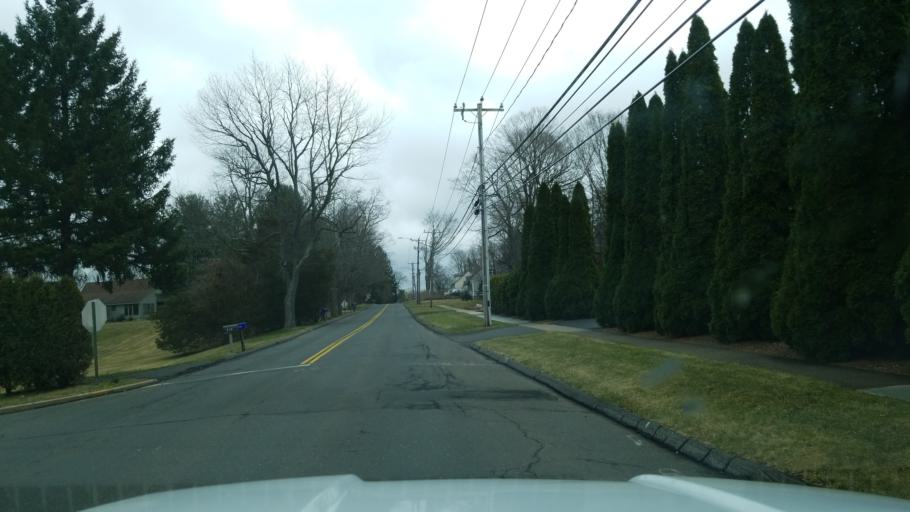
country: US
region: Connecticut
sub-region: Hartford County
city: Kensington
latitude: 41.6003
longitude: -72.7430
